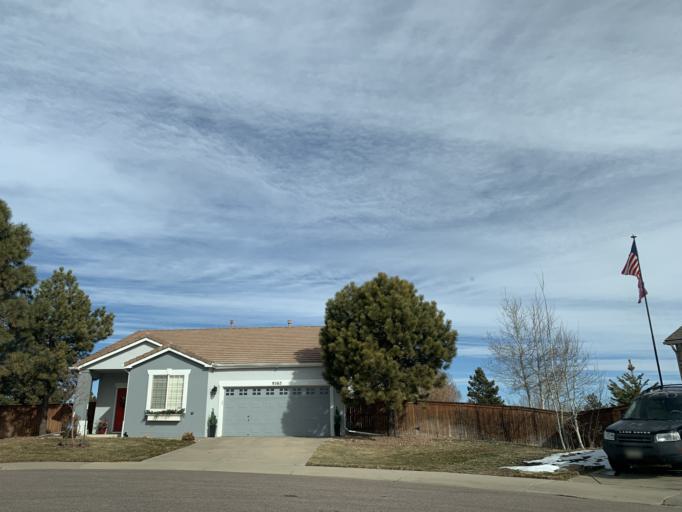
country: US
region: Colorado
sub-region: Douglas County
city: Carriage Club
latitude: 39.5419
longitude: -104.9302
